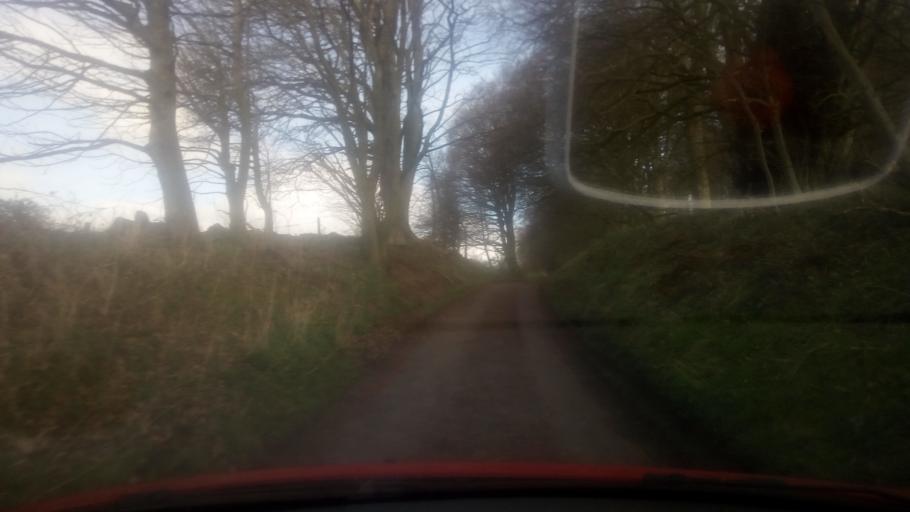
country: GB
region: Scotland
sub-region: The Scottish Borders
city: Jedburgh
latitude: 55.4957
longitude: -2.5362
